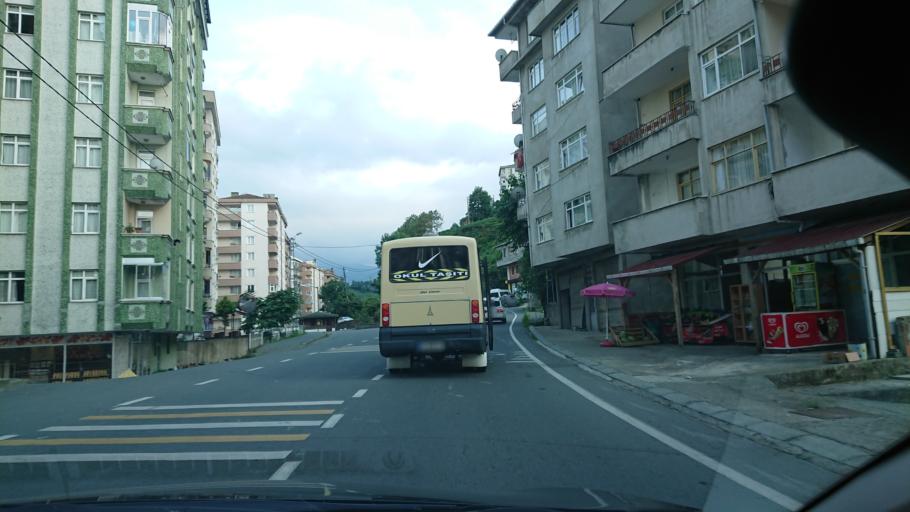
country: TR
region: Rize
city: Cayeli
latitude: 41.0810
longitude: 40.7125
